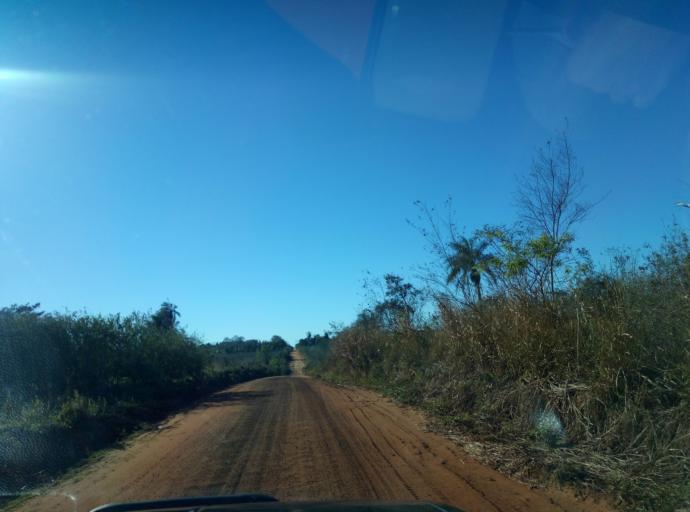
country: PY
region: Caaguazu
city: Doctor Cecilio Baez
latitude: -25.1595
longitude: -56.2866
